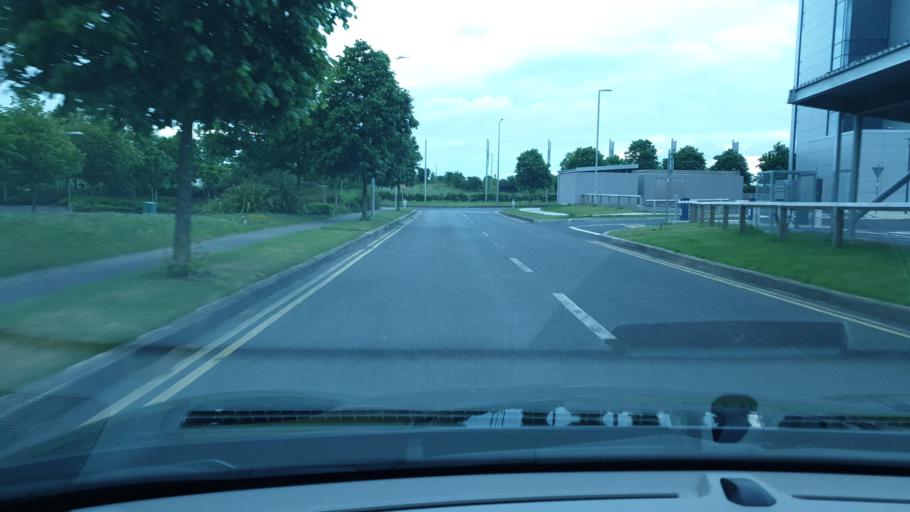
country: IE
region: Leinster
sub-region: Fingal County
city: Swords
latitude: 53.4487
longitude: -6.2191
